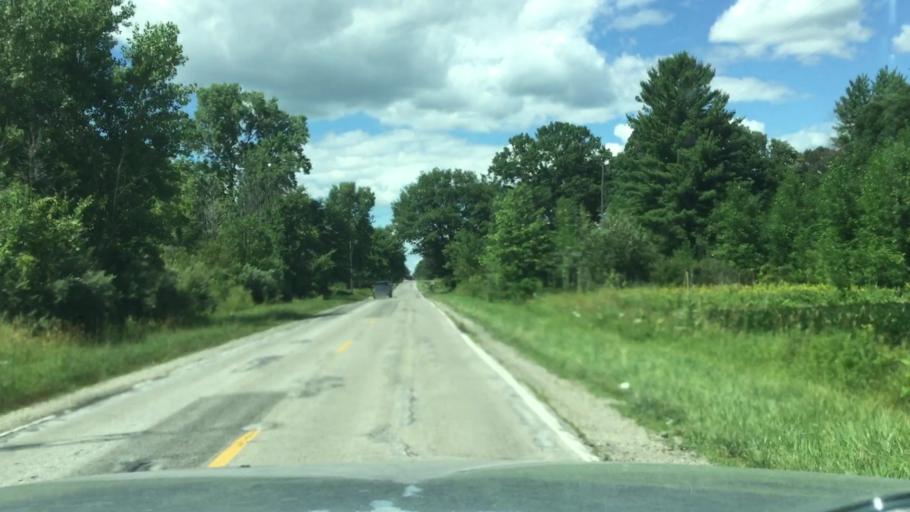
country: US
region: Michigan
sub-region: Saginaw County
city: Hemlock
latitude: 43.3697
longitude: -84.1903
